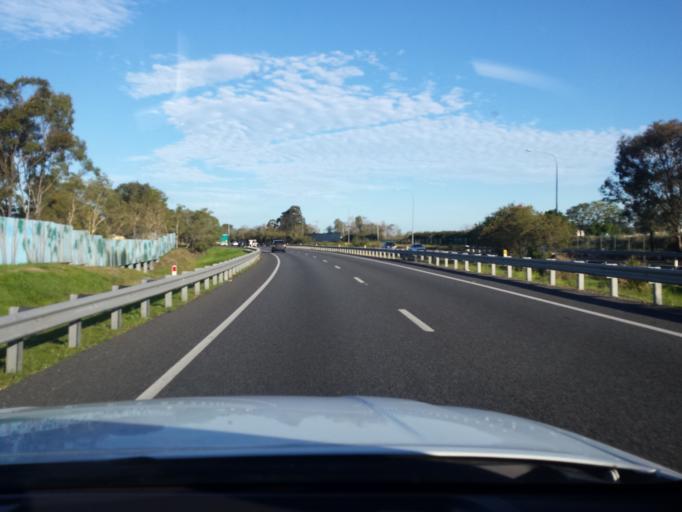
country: AU
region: Queensland
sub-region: Logan
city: Slacks Creek
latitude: -27.6824
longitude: 153.1722
